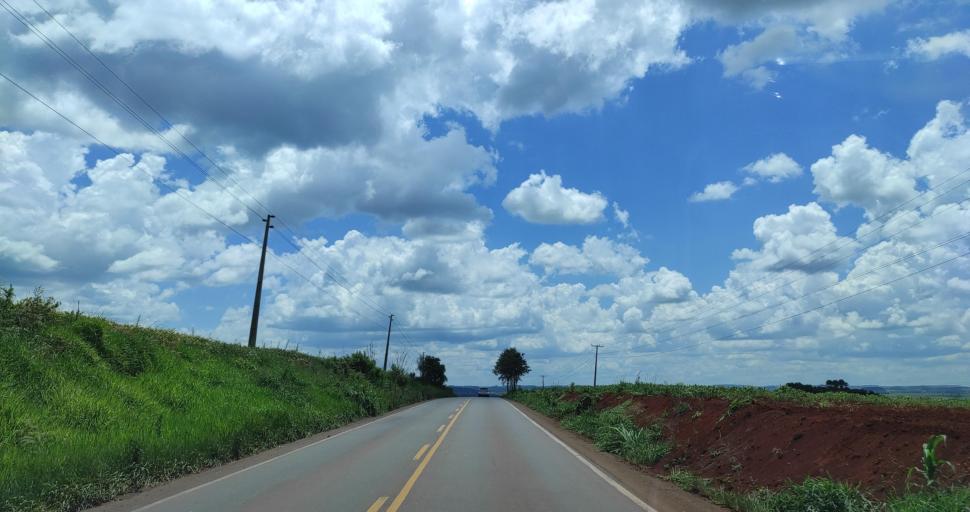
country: BR
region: Santa Catarina
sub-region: Xanxere
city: Xanxere
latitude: -26.7815
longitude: -52.4075
